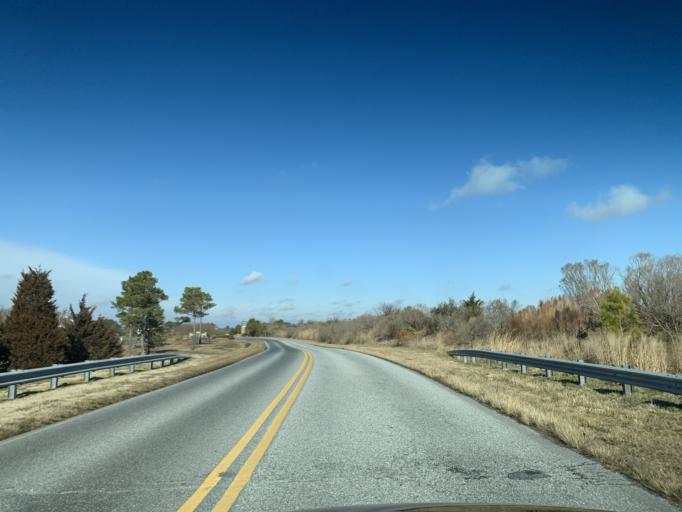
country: US
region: Maryland
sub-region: Worcester County
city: Ocean Pines
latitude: 38.4065
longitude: -75.1090
